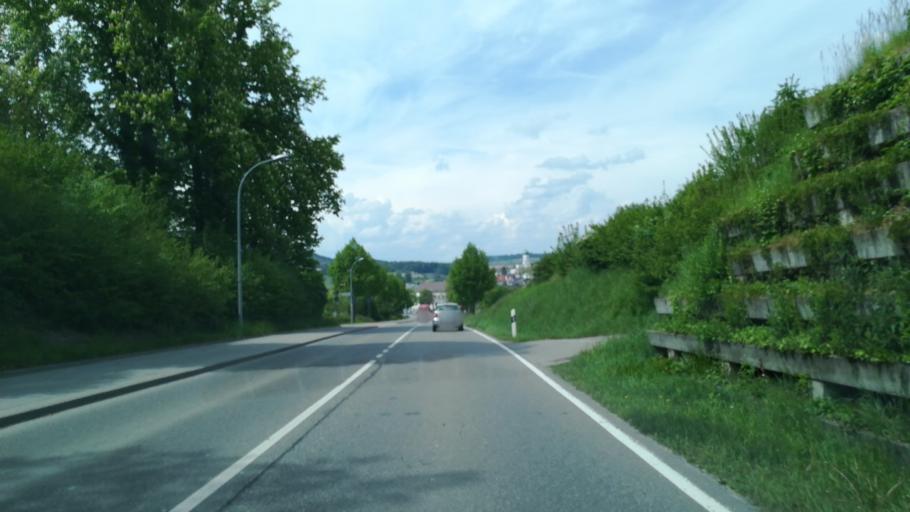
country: DE
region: Baden-Wuerttemberg
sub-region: Freiburg Region
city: Stockach
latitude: 47.8442
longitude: 9.0175
